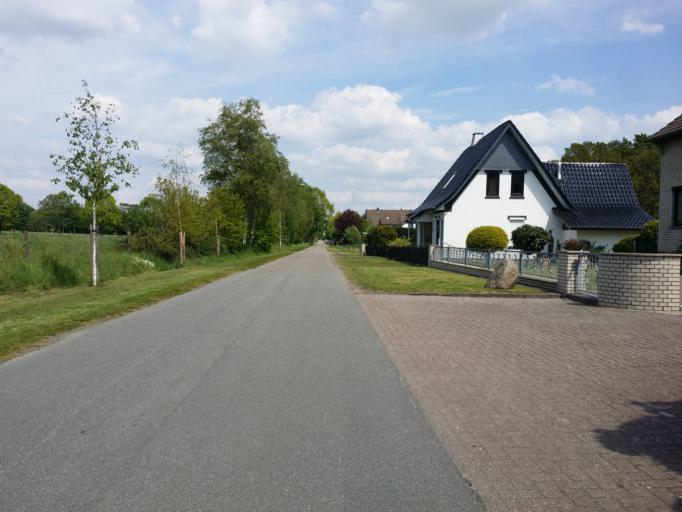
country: DE
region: Lower Saxony
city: Hambergen
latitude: 53.2884
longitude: 8.8348
